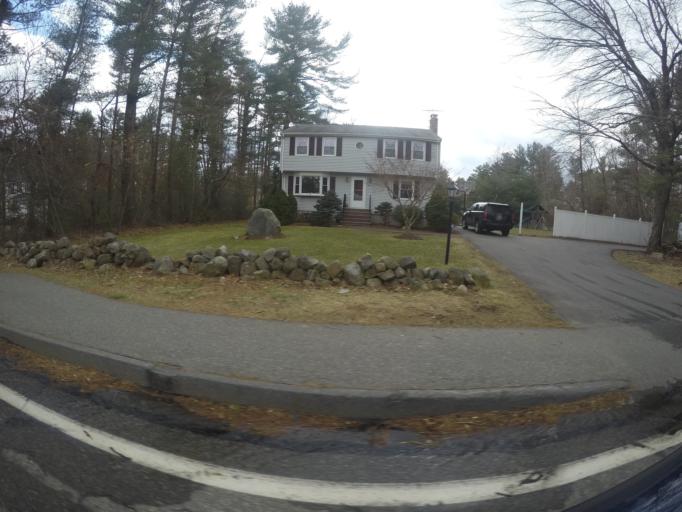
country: US
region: Massachusetts
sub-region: Bristol County
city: Easton
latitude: 42.0606
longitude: -71.1309
